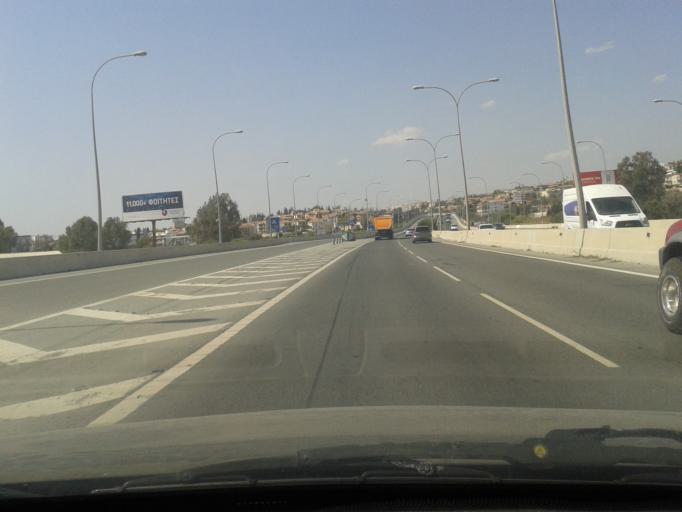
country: CY
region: Limassol
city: Mouttagiaka
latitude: 34.7067
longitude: 33.0914
